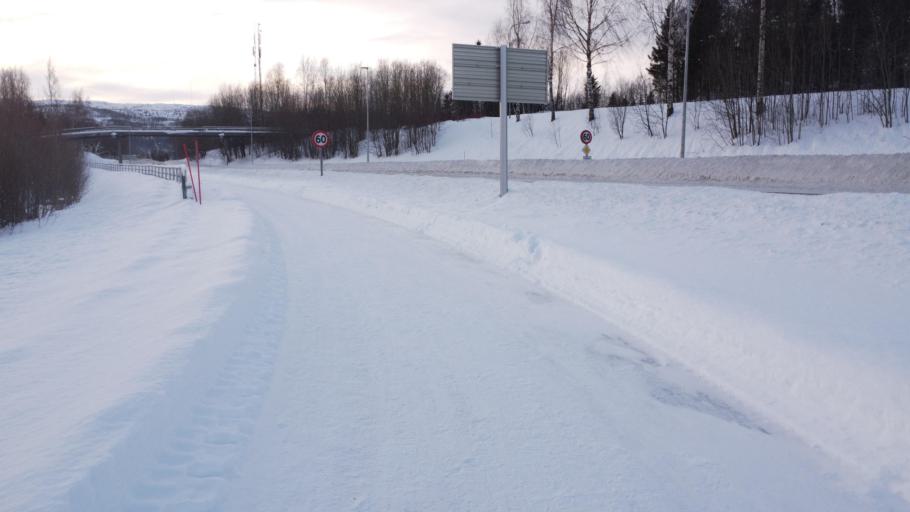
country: NO
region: Nordland
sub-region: Rana
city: Mo i Rana
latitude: 66.3277
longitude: 14.1591
